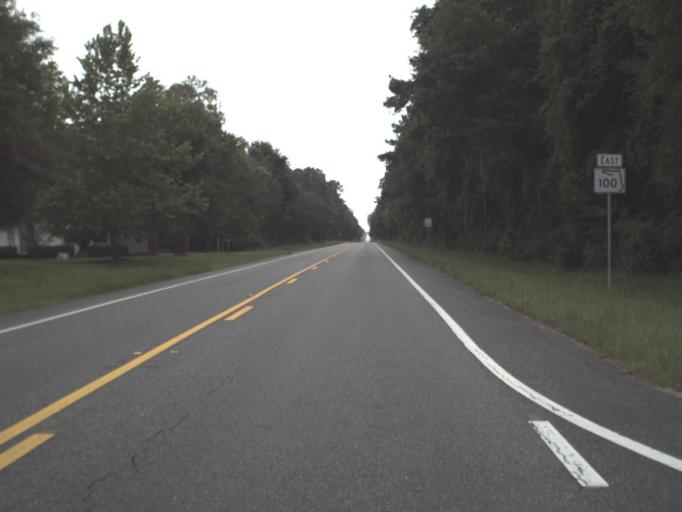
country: US
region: Florida
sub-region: Columbia County
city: Watertown
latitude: 30.1077
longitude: -82.4912
